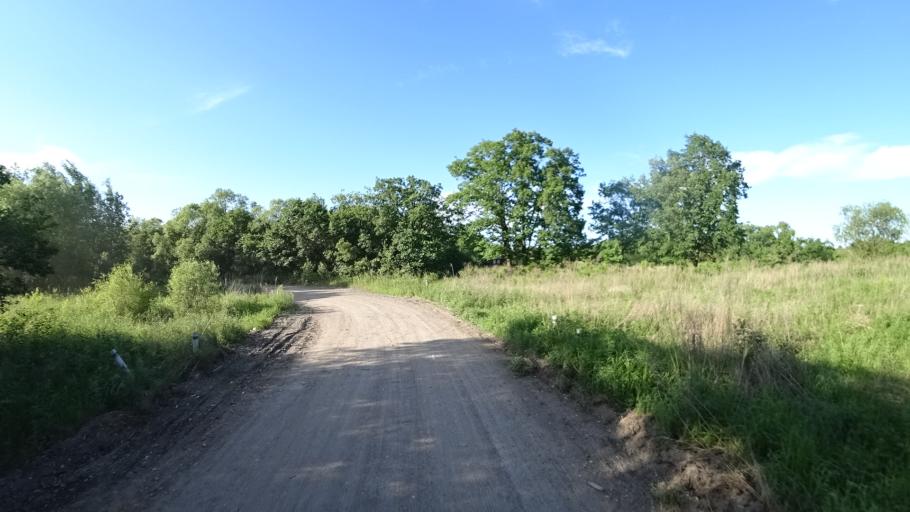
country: RU
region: Khabarovsk Krai
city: Khor
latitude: 47.8526
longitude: 134.9445
